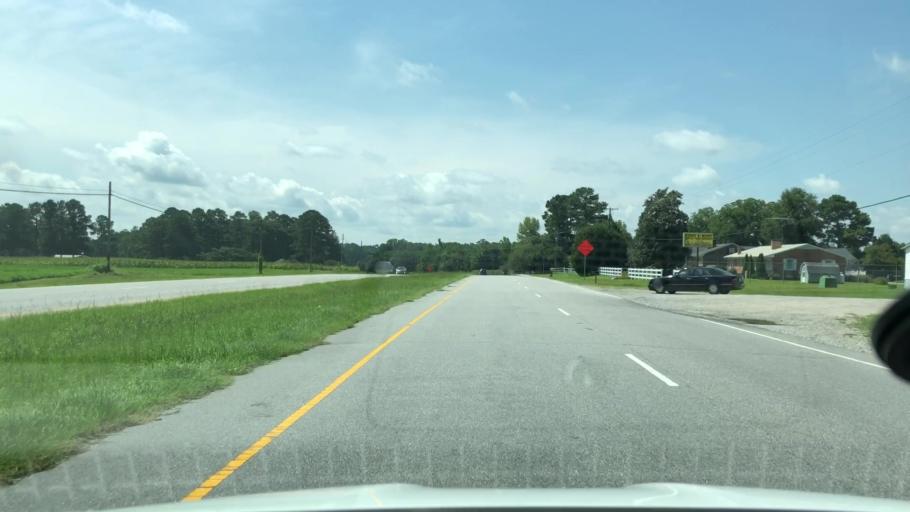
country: US
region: North Carolina
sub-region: Martin County
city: Williamston
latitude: 35.7959
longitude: -77.0599
